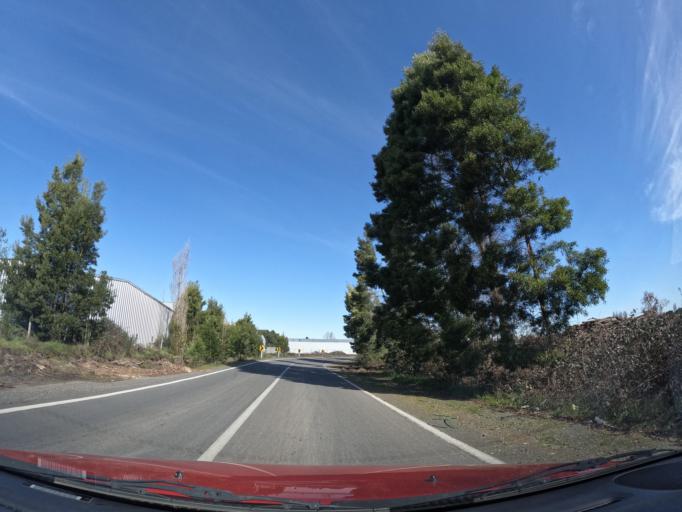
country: CL
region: Biobio
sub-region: Provincia de Biobio
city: Cabrero
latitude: -37.0388
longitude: -72.3735
